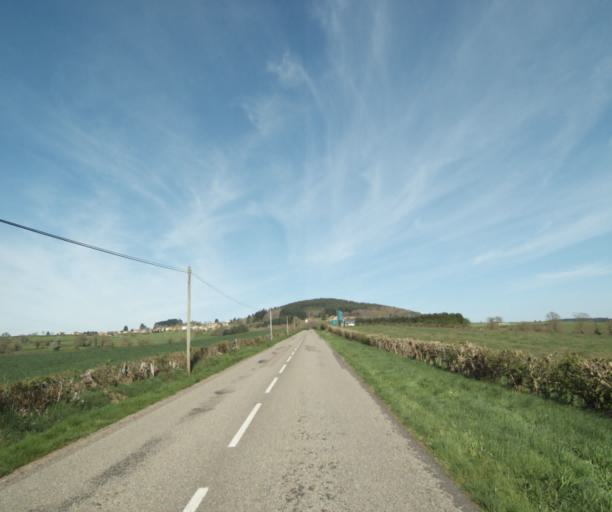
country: FR
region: Bourgogne
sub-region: Departement de Saone-et-Loire
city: Charolles
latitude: 46.3939
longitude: 4.3883
